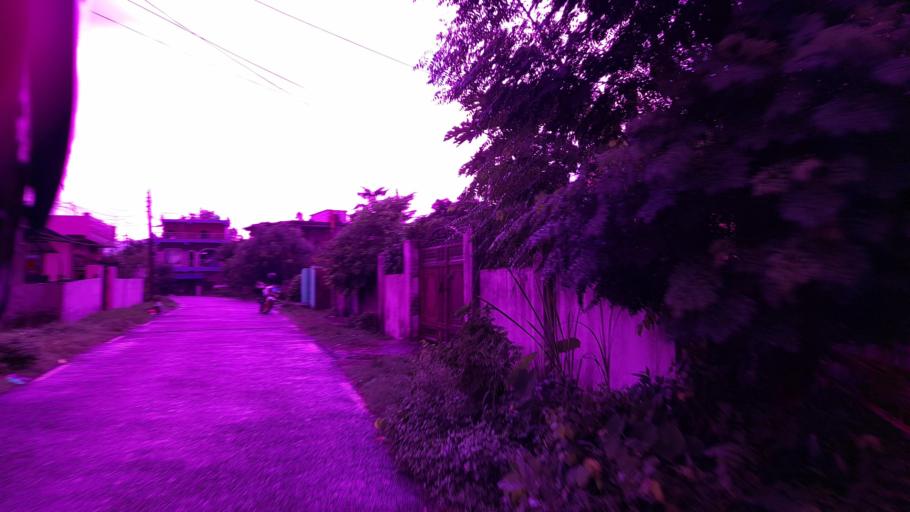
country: NP
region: Mid Western
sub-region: Bheri Zone
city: Nepalgunj
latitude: 28.1948
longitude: 81.6980
